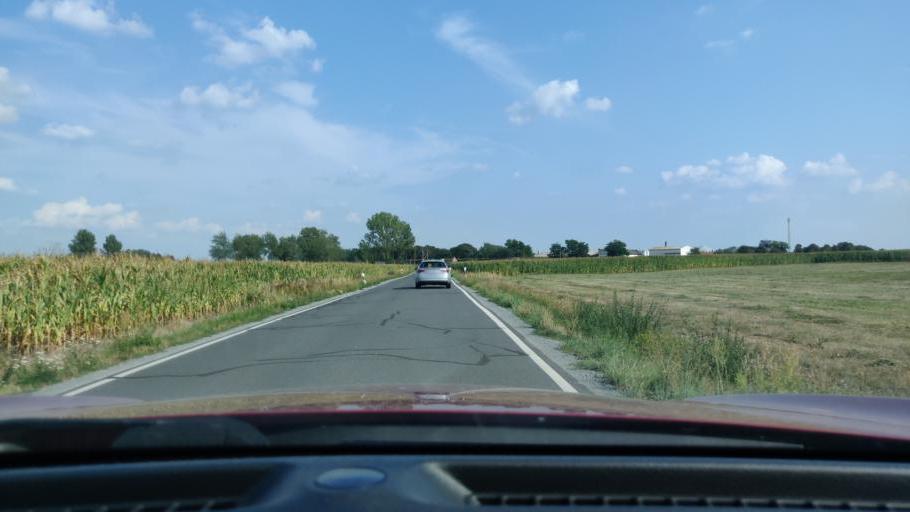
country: DE
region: Saxony
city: Mockrehna
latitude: 51.4890
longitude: 12.8634
